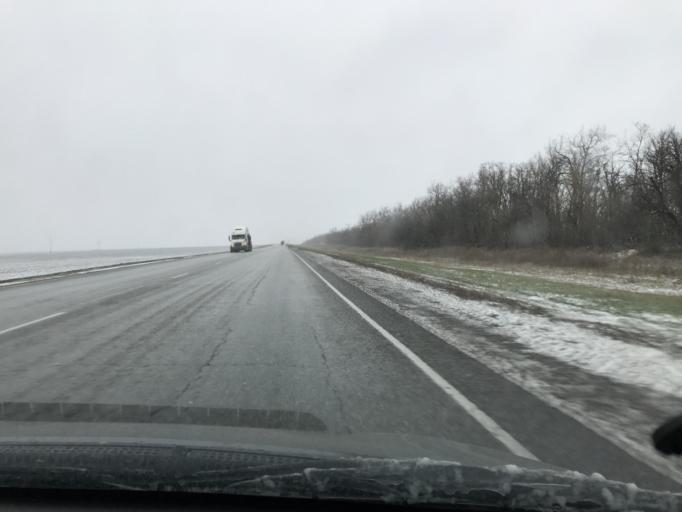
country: RU
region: Rostov
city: Mechetinskaya
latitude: 46.6847
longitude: 40.5190
